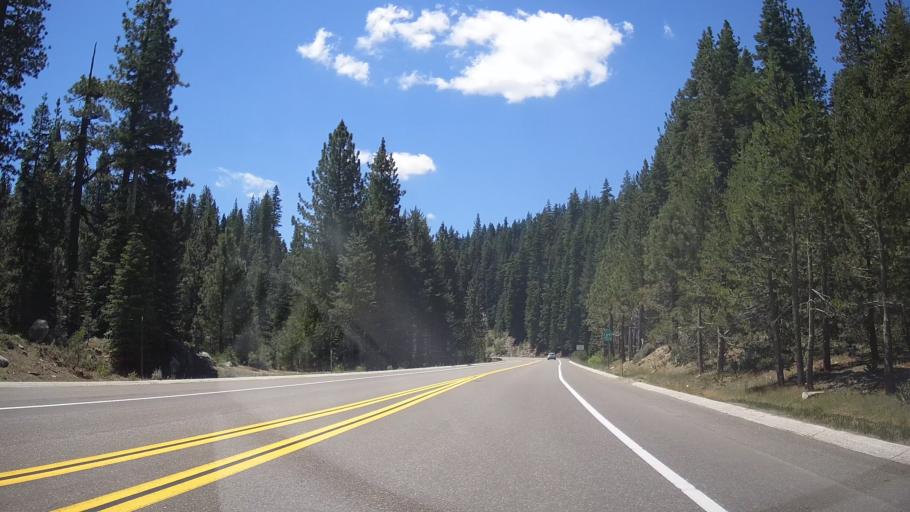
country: US
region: California
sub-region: Placer County
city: Sunnyside-Tahoe City
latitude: 39.2030
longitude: -120.2005
